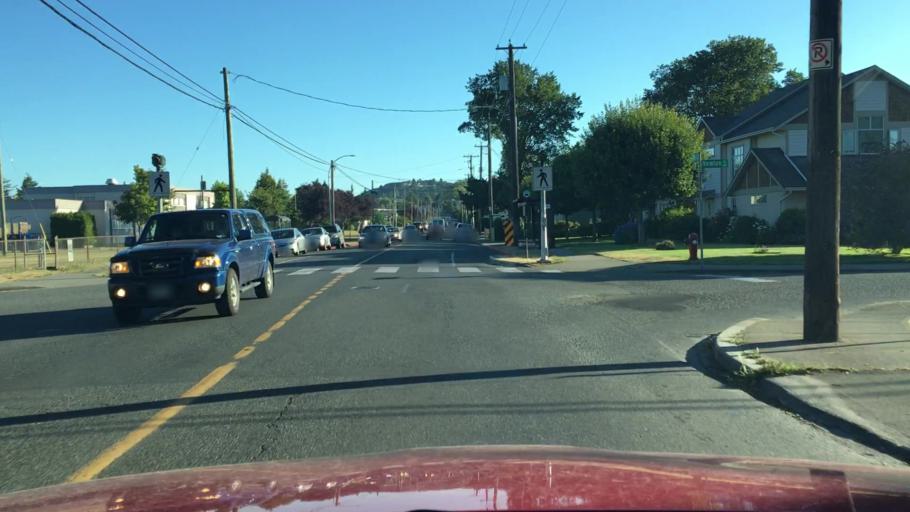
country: CA
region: British Columbia
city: Oak Bay
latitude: 48.4387
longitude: -123.3281
